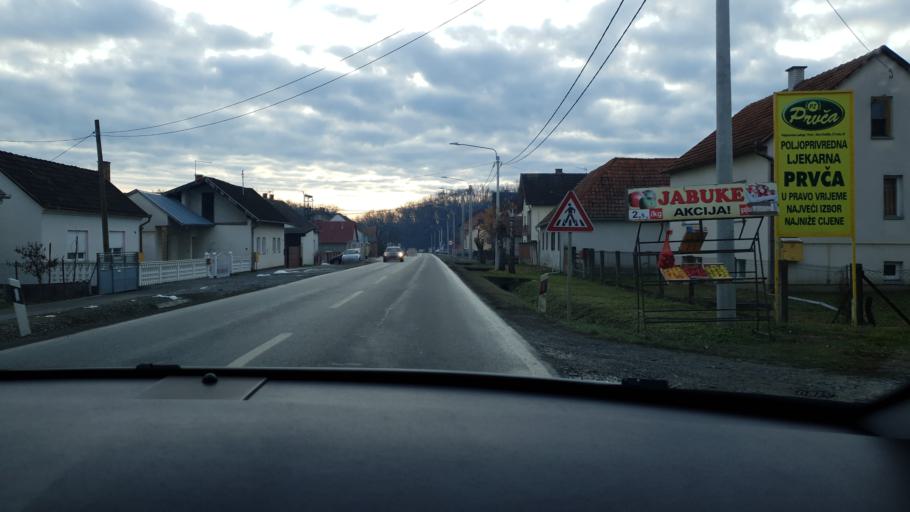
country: HR
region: Pozesko-Slavonska
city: Vidovci
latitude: 45.3529
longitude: 17.7244
